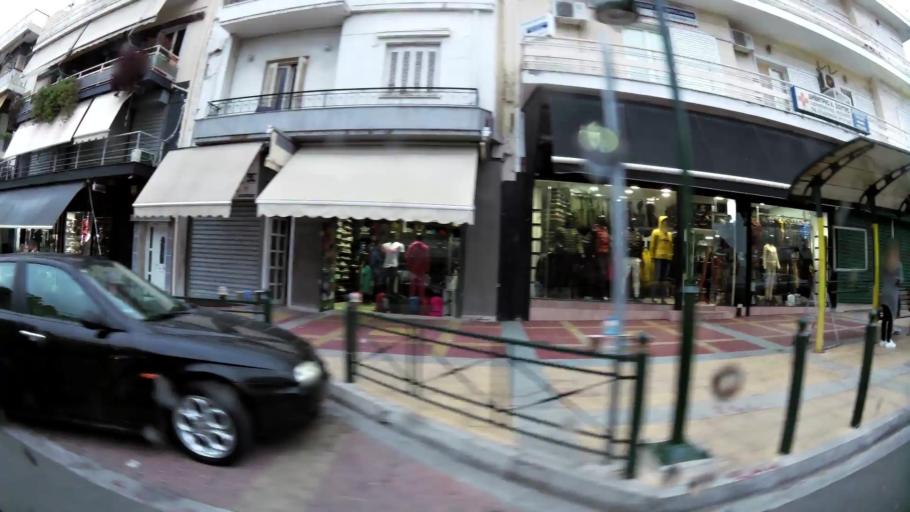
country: GR
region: Attica
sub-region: Nomarchia Athinas
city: Agia Varvara
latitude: 37.9906
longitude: 23.6593
